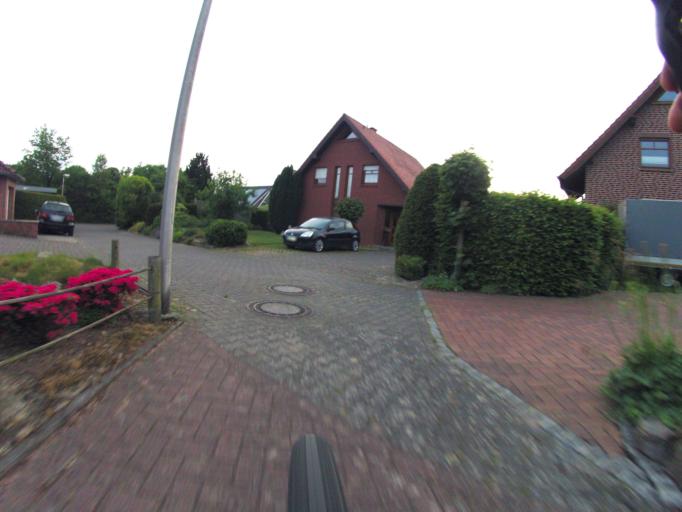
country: DE
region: North Rhine-Westphalia
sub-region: Regierungsbezirk Munster
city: Tecklenburg
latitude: 52.2667
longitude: 7.7954
